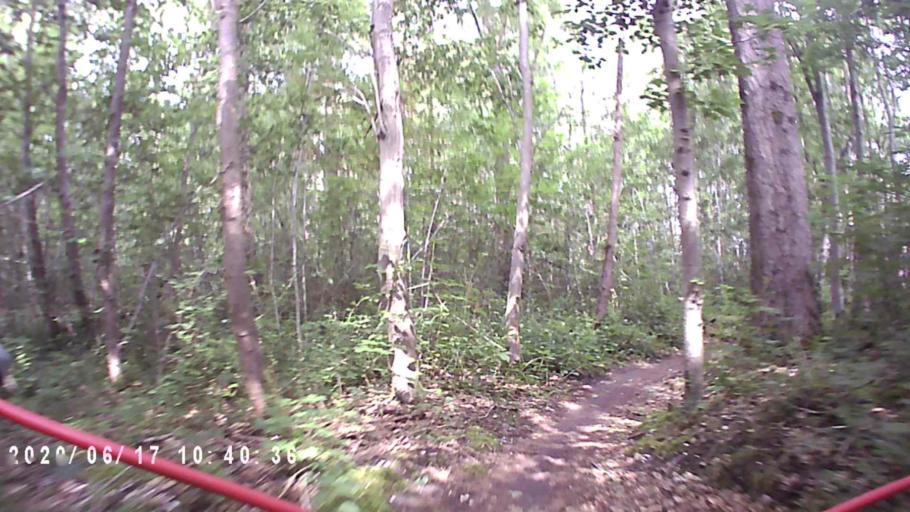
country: NL
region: Friesland
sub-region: Gemeente Dongeradeel
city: Anjum
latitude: 53.4041
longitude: 6.2308
